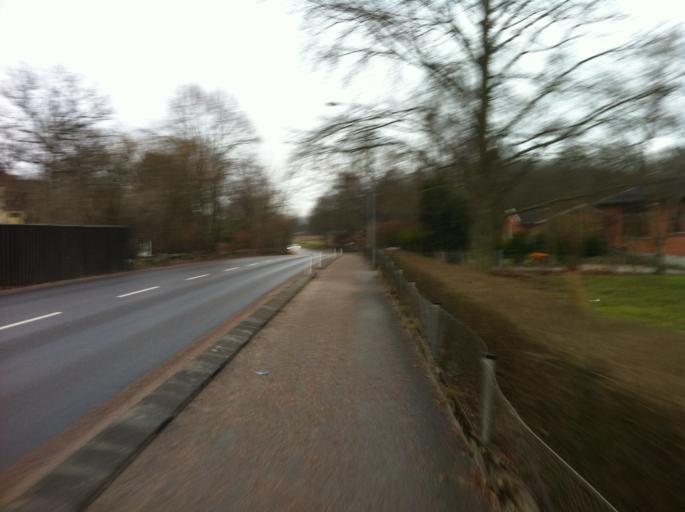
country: SE
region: Skane
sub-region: Hoors Kommun
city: Satofta
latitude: 55.9145
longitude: 13.5474
